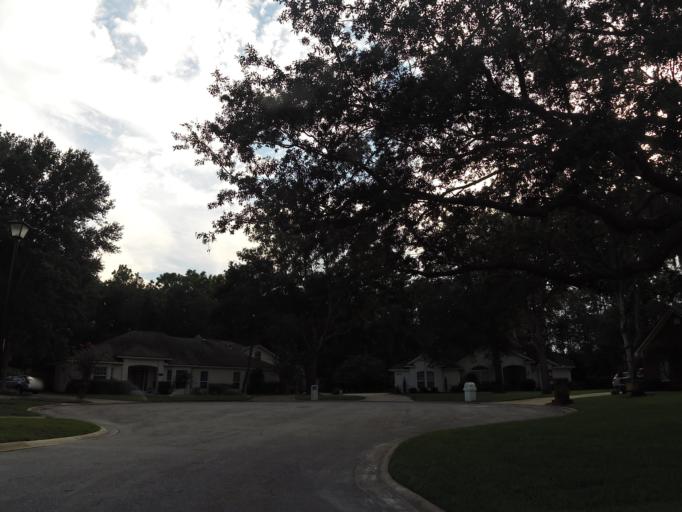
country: US
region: Florida
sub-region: Saint Johns County
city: Fruit Cove
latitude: 30.0924
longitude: -81.6164
